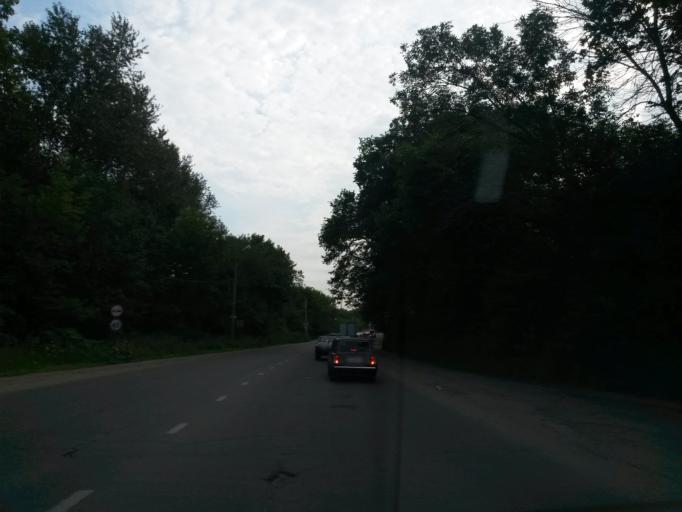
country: RU
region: Jaroslavl
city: Yaroslavl
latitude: 57.6118
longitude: 39.8391
